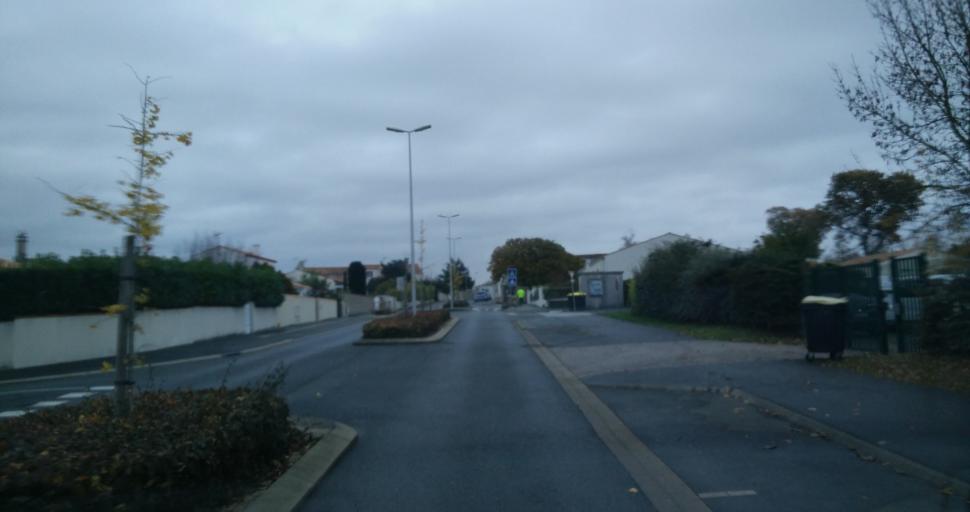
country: FR
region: Poitou-Charentes
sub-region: Departement de la Charente-Maritime
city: Puilboreau
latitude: 46.1884
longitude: -1.1211
